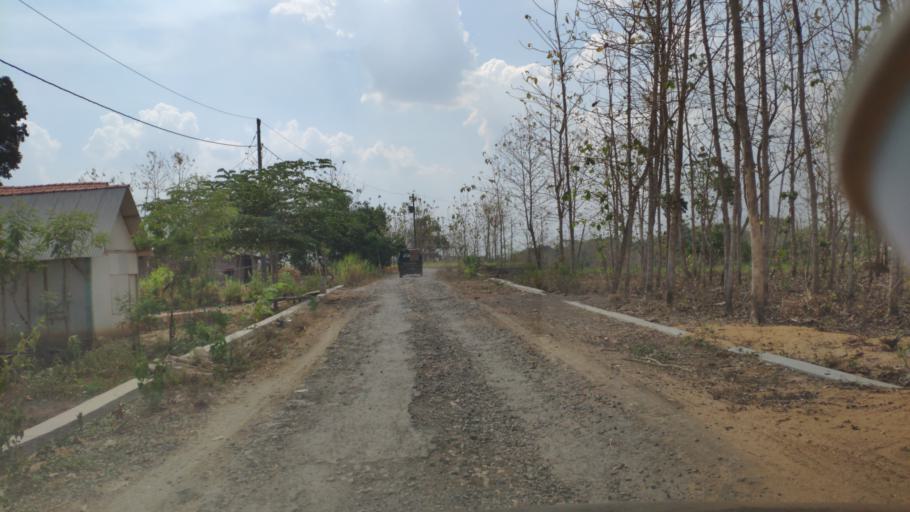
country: ID
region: Central Java
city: Krocok
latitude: -6.9780
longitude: 111.2811
